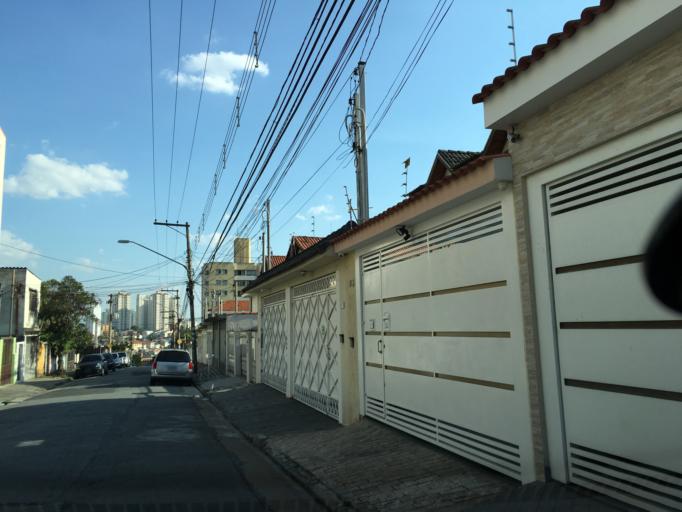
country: BR
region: Sao Paulo
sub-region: Sao Paulo
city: Sao Paulo
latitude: -23.4696
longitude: -46.6318
